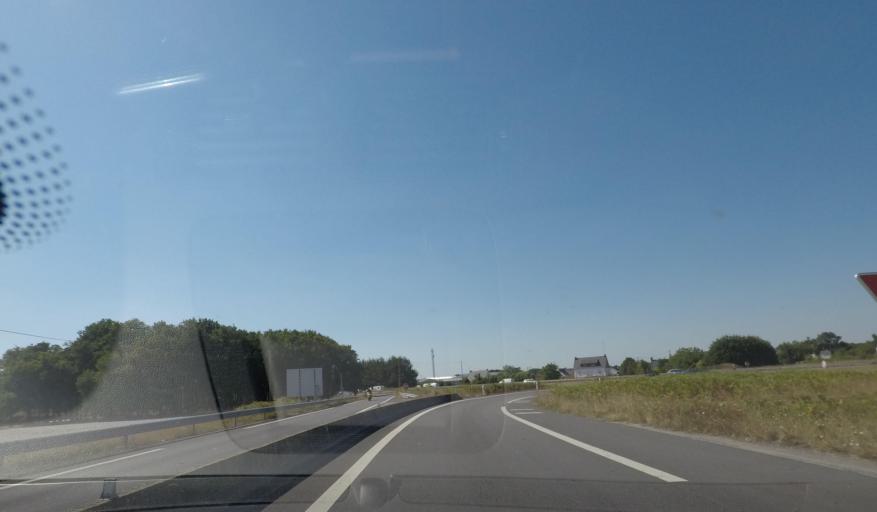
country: FR
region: Brittany
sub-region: Departement du Morbihan
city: Peaule
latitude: 47.5357
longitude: -2.3973
